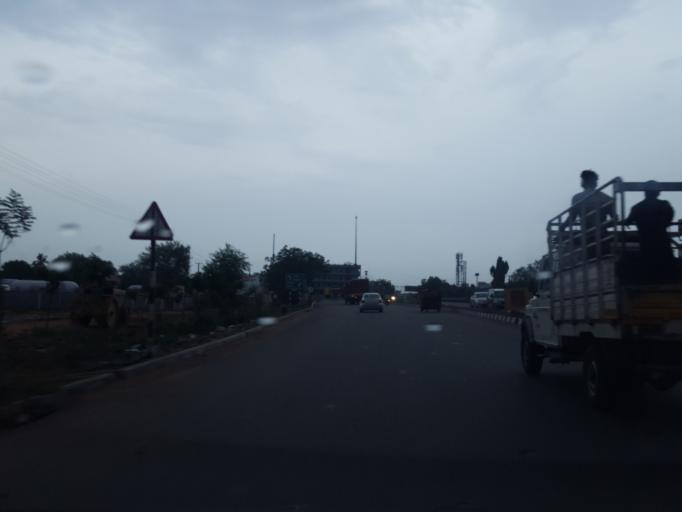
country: IN
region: Telangana
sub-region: Mahbubnagar
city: Farrukhnagar
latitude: 17.1521
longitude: 78.2911
